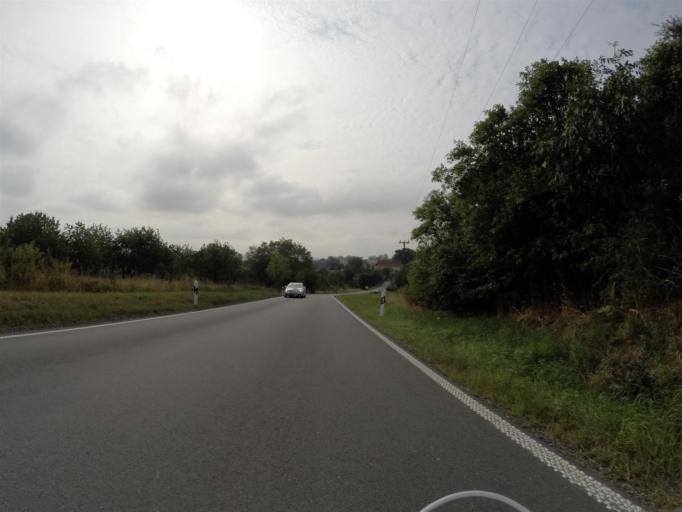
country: DE
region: Thuringia
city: Schongleina
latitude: 50.9304
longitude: 11.7204
